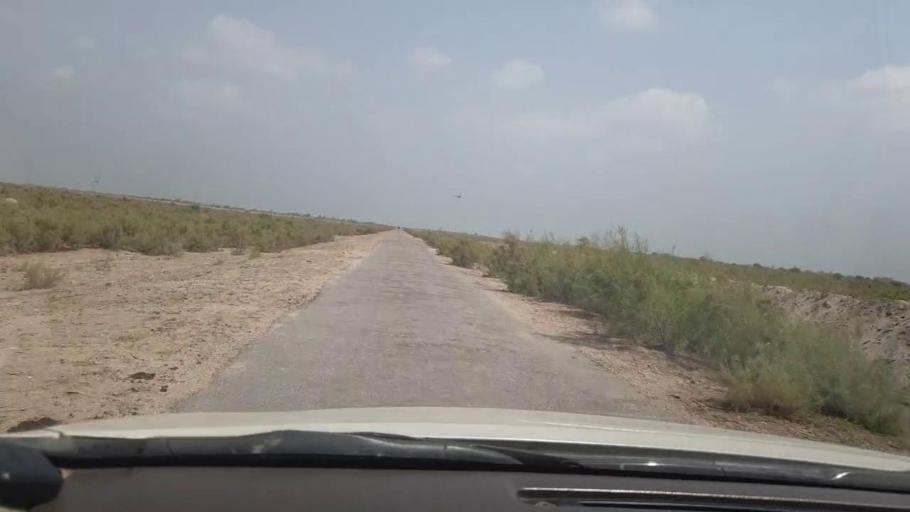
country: PK
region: Sindh
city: Garhi Yasin
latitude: 28.0205
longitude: 68.5003
